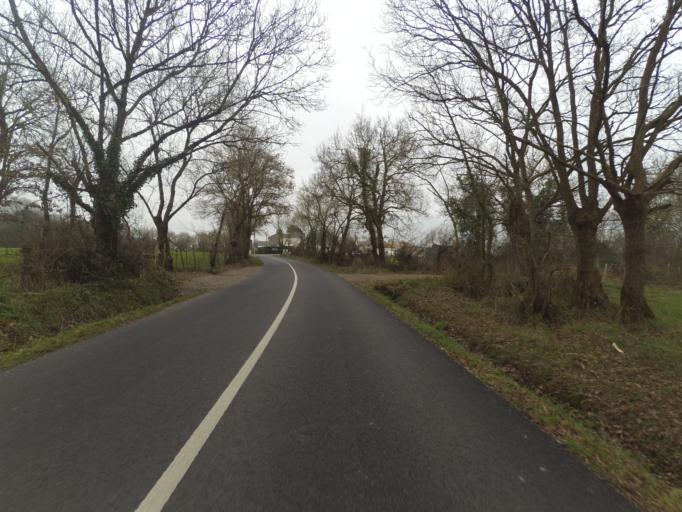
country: FR
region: Pays de la Loire
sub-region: Departement de la Loire-Atlantique
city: Indre
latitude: 47.2264
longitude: -1.6821
